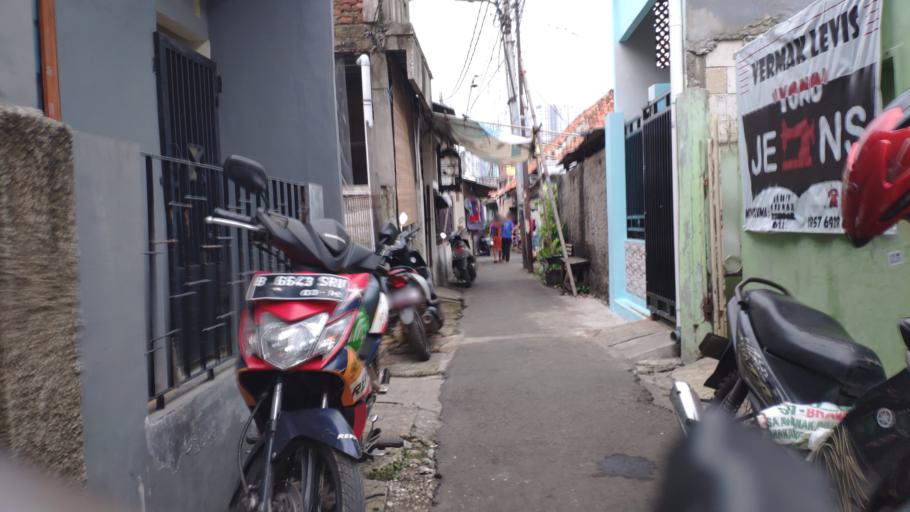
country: ID
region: Jakarta Raya
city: Jakarta
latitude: -6.2171
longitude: 106.8397
